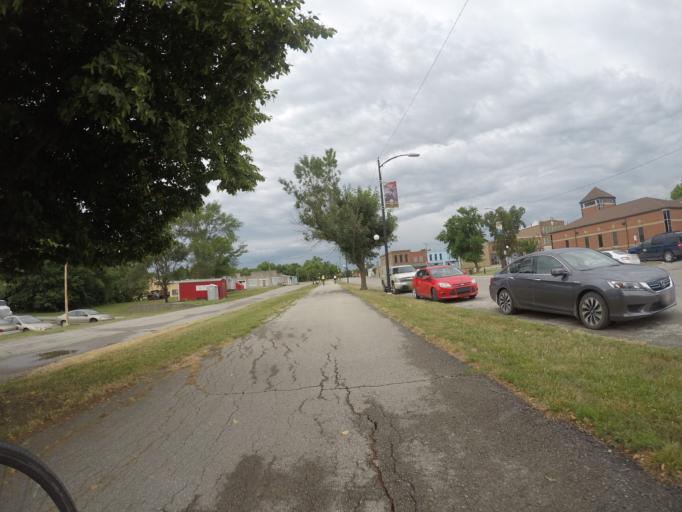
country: US
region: Kansas
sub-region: Anderson County
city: Garnett
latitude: 38.2806
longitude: -95.2401
